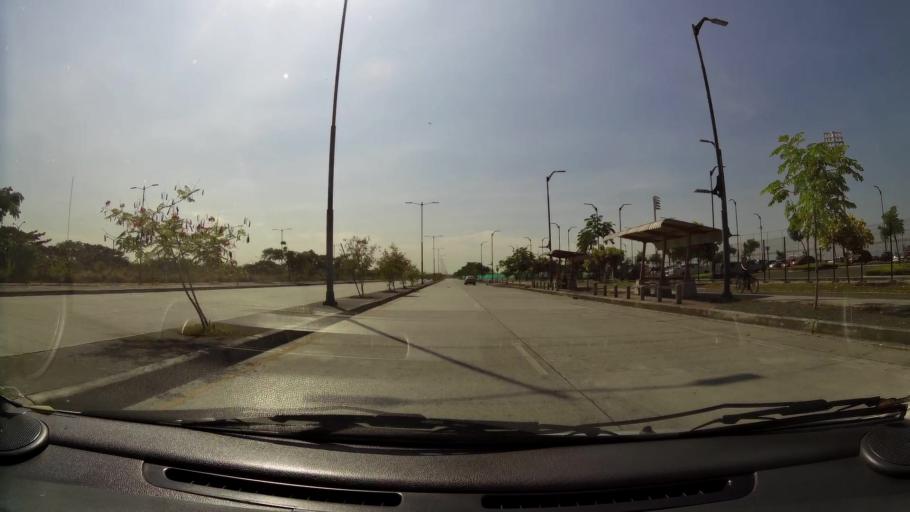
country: EC
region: Guayas
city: Eloy Alfaro
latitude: -2.1012
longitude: -79.9023
